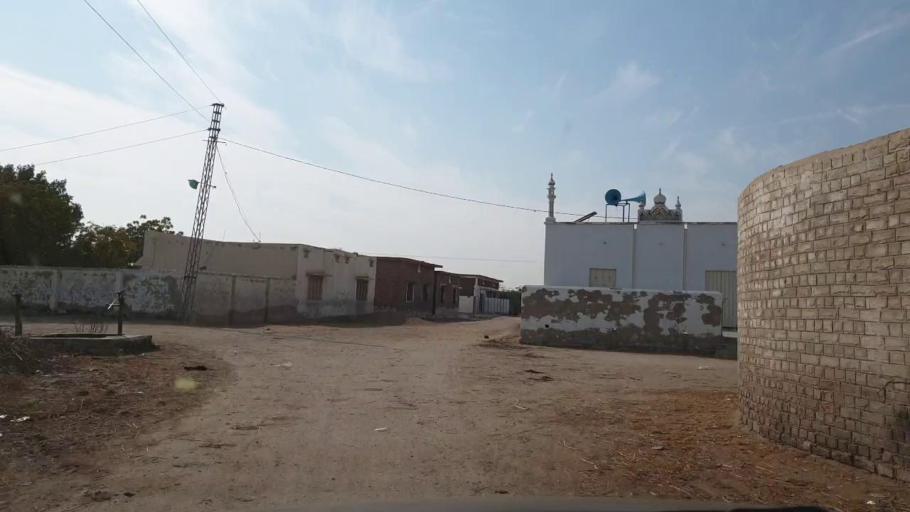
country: PK
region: Sindh
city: Khadro
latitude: 26.1251
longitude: 68.7194
